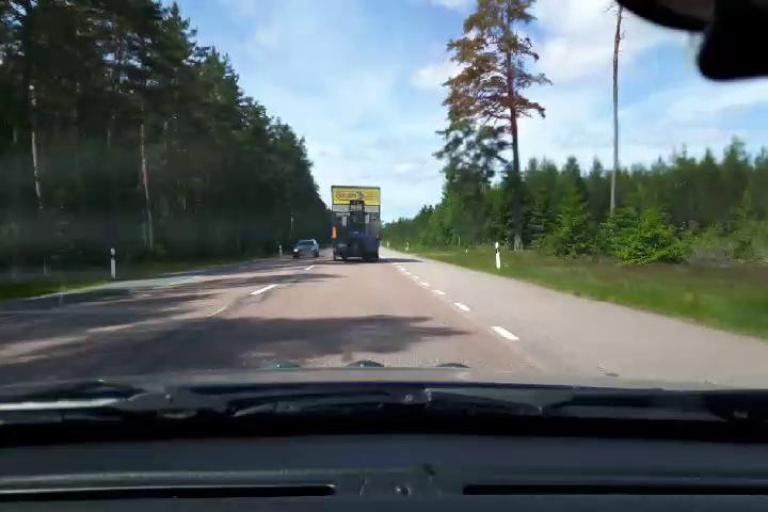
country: SE
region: Uppsala
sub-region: Osthammars Kommun
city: Bjorklinge
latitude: 60.1155
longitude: 17.5201
